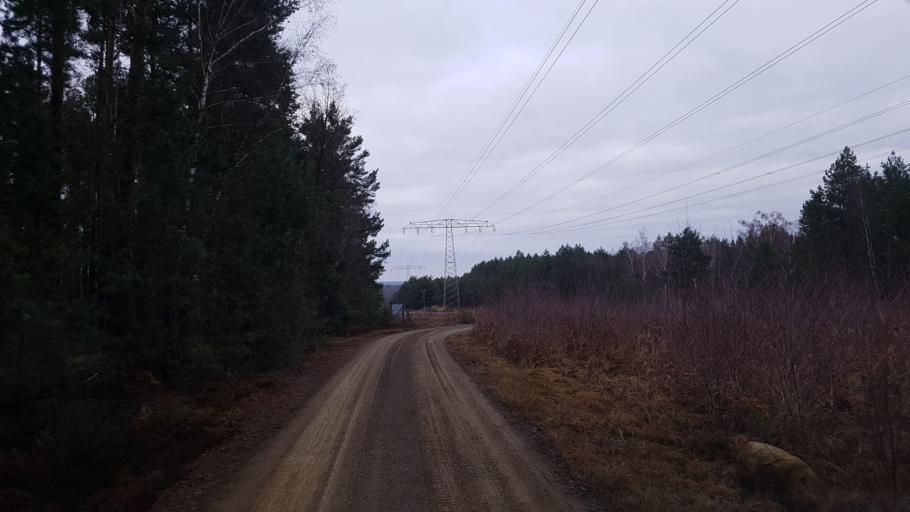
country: DE
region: Brandenburg
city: Altdobern
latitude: 51.6434
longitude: 14.0046
